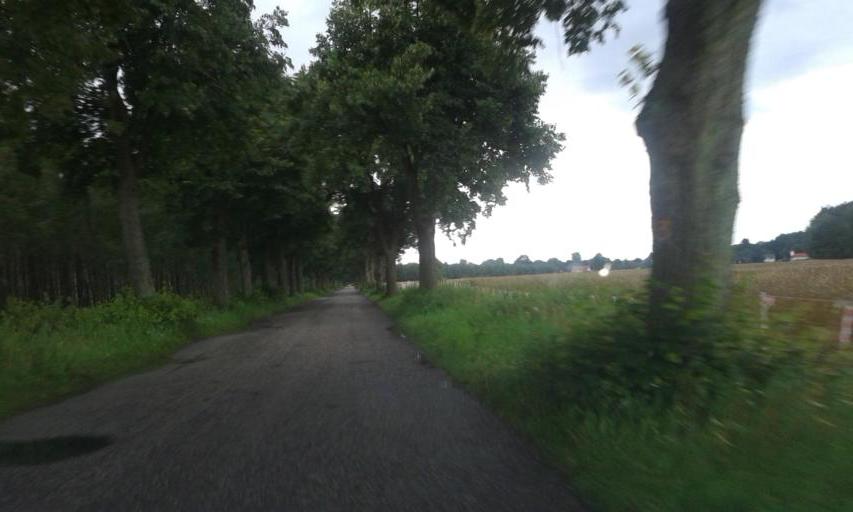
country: PL
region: Greater Poland Voivodeship
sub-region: Powiat zlotowski
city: Sypniewo
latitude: 53.4693
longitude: 16.5098
